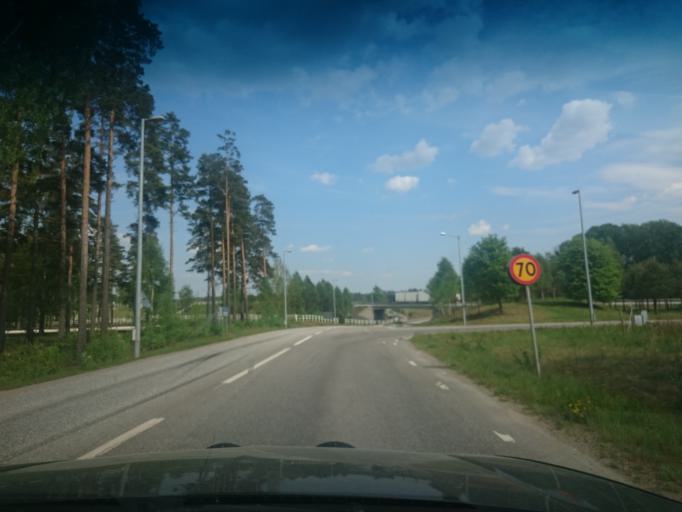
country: SE
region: Joenkoeping
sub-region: Vetlanda Kommun
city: Vetlanda
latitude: 57.4200
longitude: 15.1075
